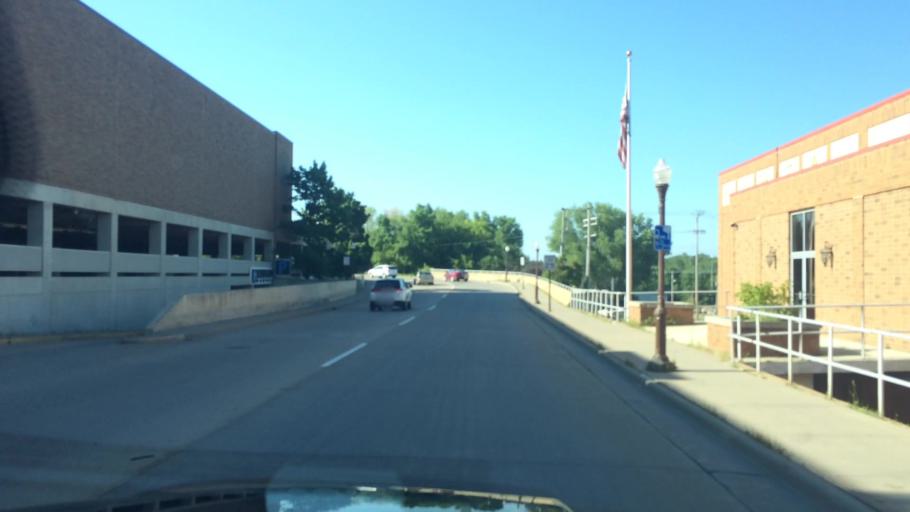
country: US
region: Wisconsin
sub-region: Marathon County
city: Wausau
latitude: 44.9585
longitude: -89.6305
